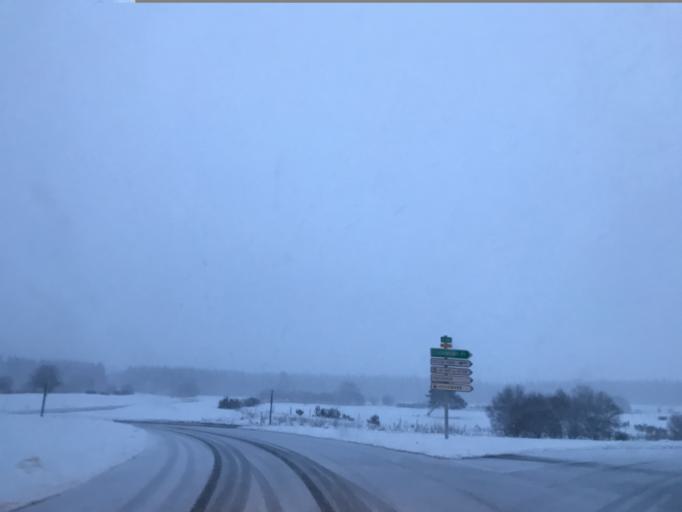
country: FR
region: Auvergne
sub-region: Departement du Puy-de-Dome
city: Saint-Sauves-d'Auvergne
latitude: 45.6552
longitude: 2.6905
